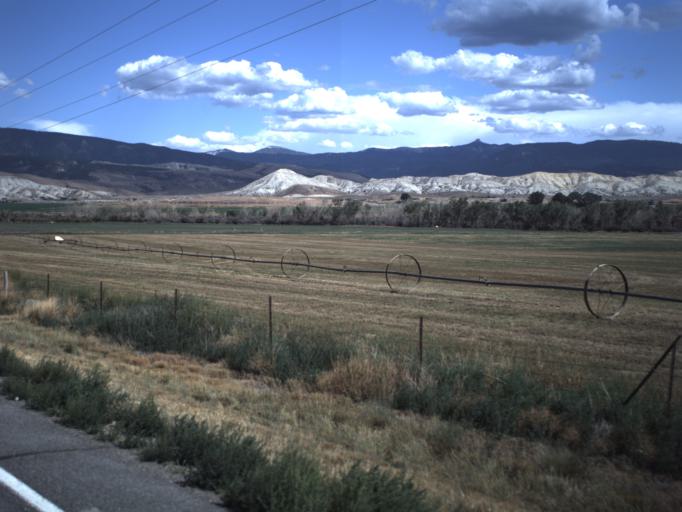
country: US
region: Utah
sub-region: Sanpete County
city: Gunnison
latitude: 39.1551
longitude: -111.7678
